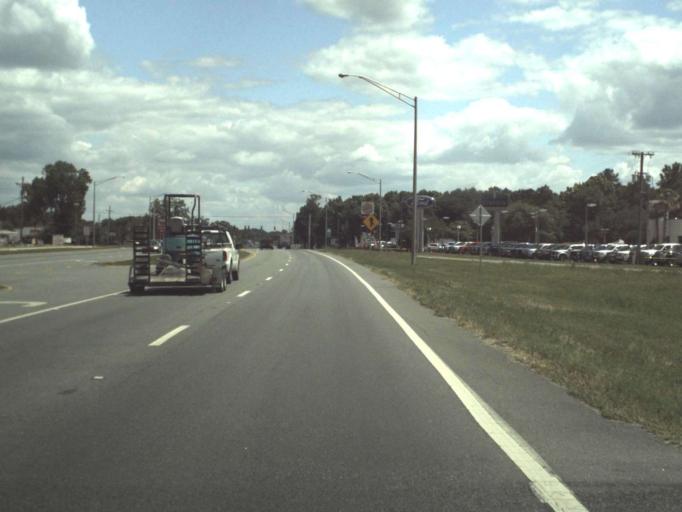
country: US
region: Florida
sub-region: Marion County
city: Ocala
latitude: 29.2176
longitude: -82.1460
